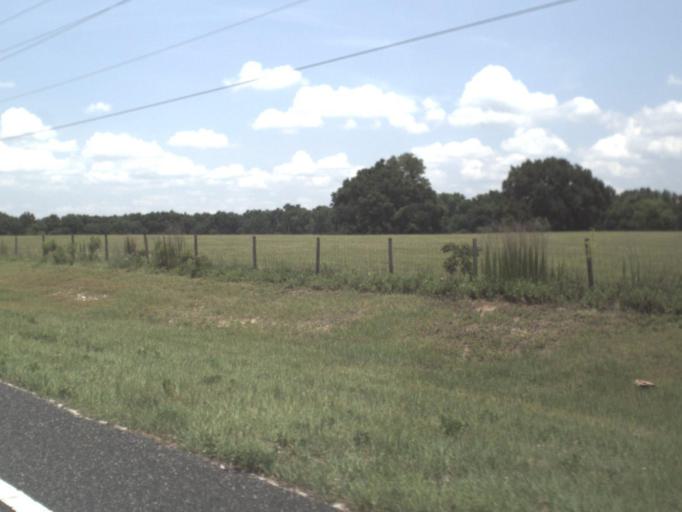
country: US
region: Florida
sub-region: Alachua County
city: Newberry
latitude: 29.6549
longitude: -82.5591
